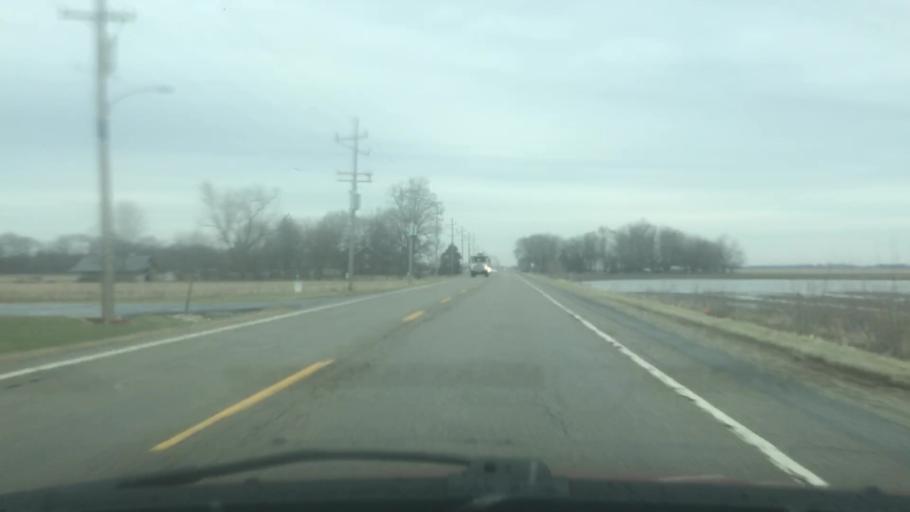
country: US
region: Indiana
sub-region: Porter County
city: Kouts
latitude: 41.3253
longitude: -87.0259
